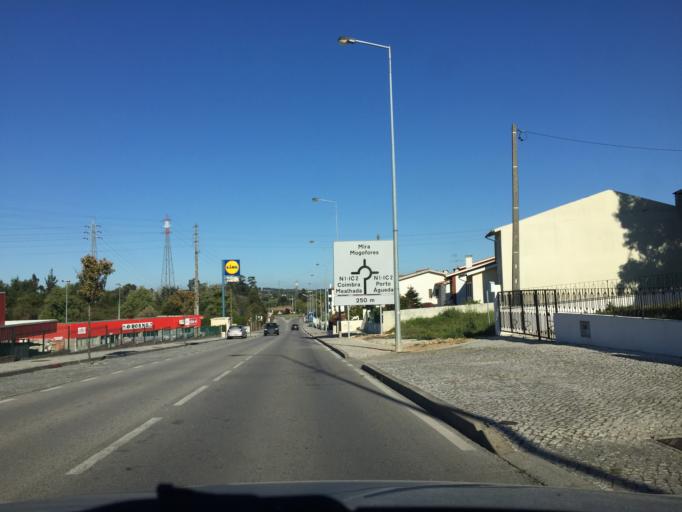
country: PT
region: Aveiro
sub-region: Anadia
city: Arcos
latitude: 40.4424
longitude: -8.4486
